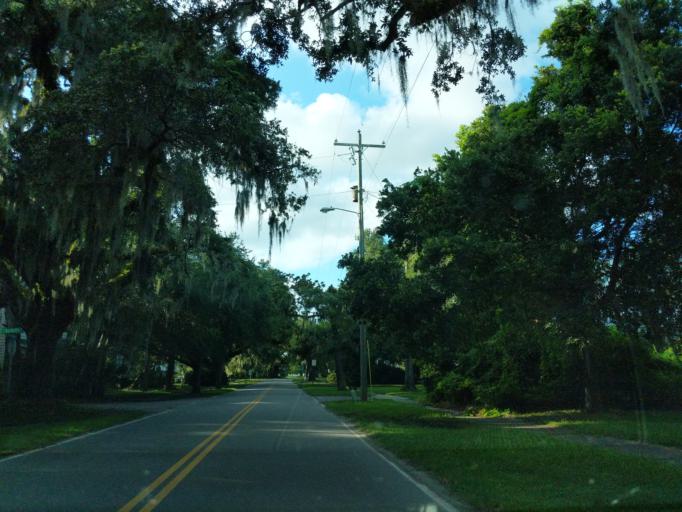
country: US
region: South Carolina
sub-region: Charleston County
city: Awendaw
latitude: 33.0845
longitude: -79.4601
